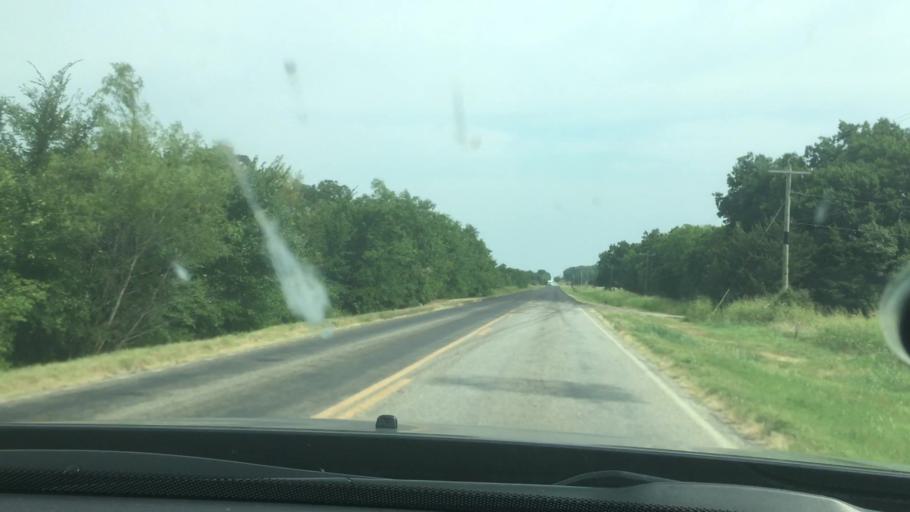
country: US
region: Oklahoma
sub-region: Coal County
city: Coalgate
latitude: 34.3523
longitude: -96.4246
